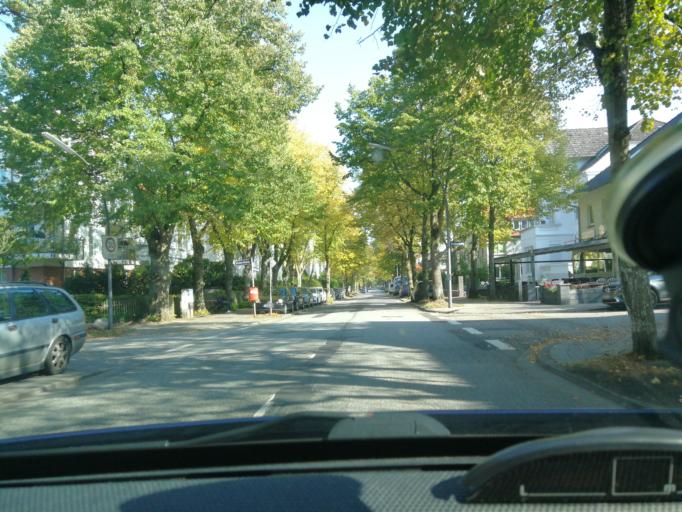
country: DE
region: Hamburg
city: Harburg
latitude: 53.4632
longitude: 9.9526
